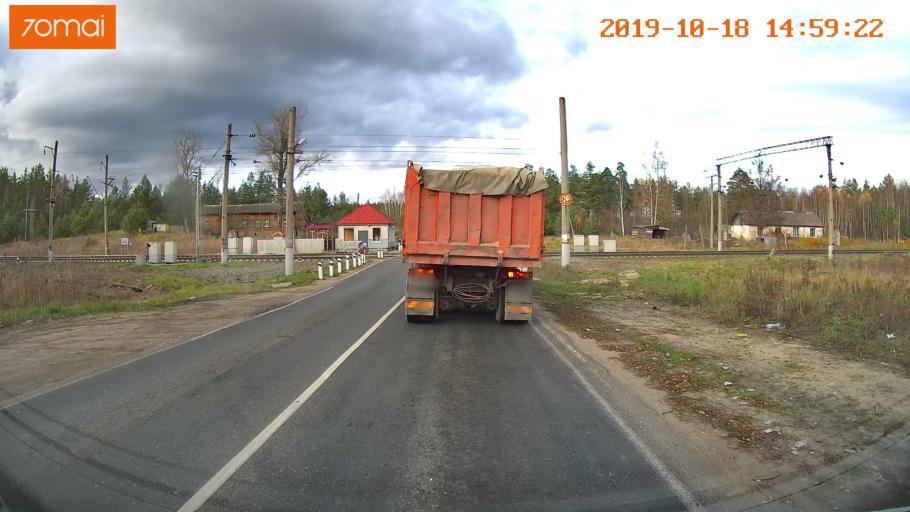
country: RU
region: Vladimir
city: Kurlovo
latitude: 55.4979
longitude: 40.5741
